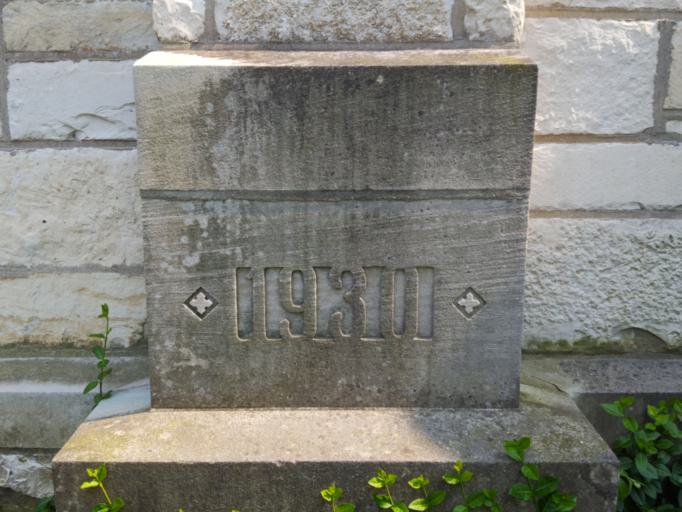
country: US
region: Illinois
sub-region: Lake County
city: Highland Park
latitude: 42.1847
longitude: -87.7972
